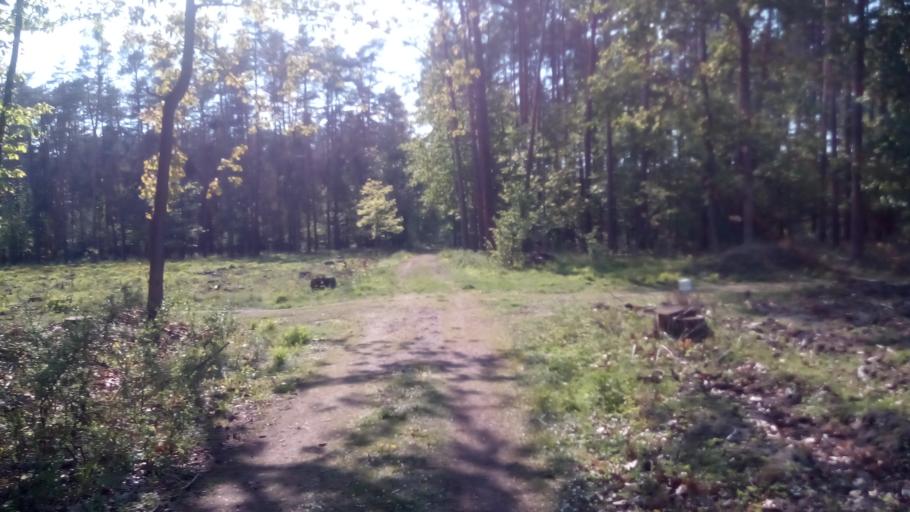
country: PL
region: Opole Voivodeship
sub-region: Powiat opolski
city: Tarnow Opolski
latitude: 50.5846
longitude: 18.0713
